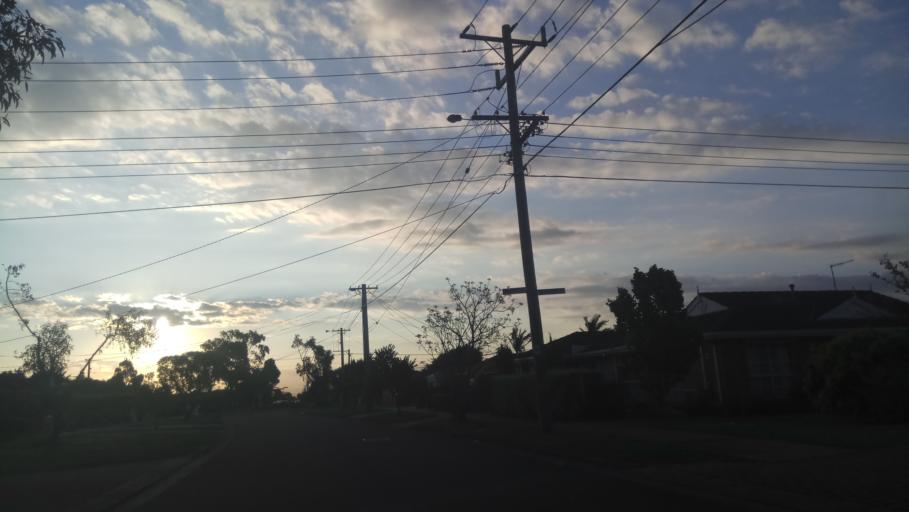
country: AU
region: Victoria
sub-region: Hobsons Bay
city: Altona Meadows
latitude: -37.8776
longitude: 144.7848
